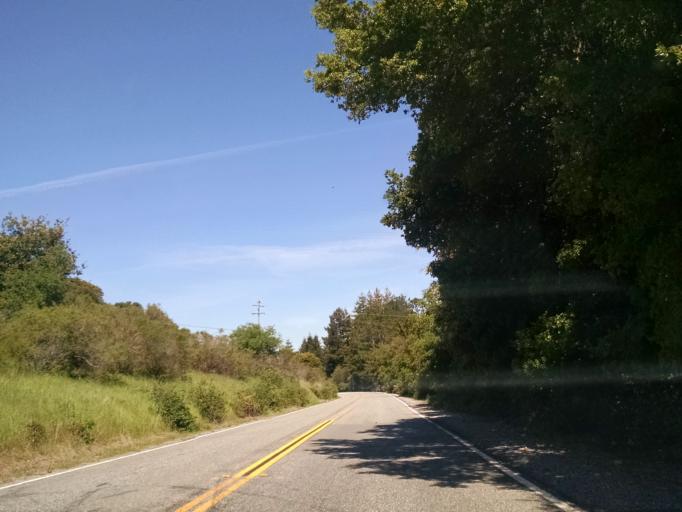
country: US
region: California
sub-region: San Mateo County
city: Portola Valley
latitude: 37.3295
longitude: -122.2102
